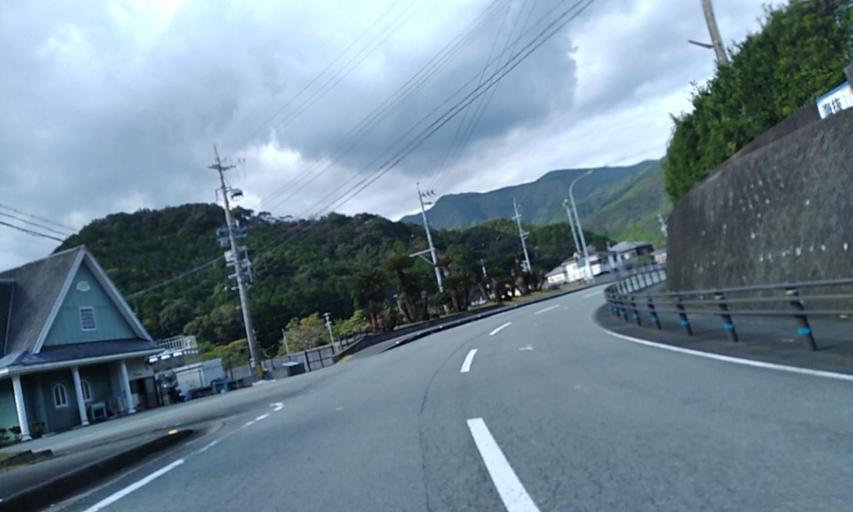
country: JP
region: Mie
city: Owase
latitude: 34.2247
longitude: 136.3944
